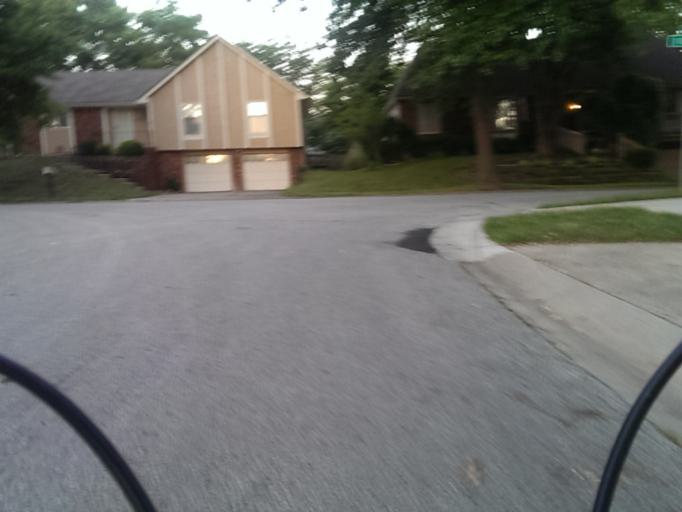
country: US
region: Missouri
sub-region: Jackson County
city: Grandview
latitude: 38.9122
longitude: -94.5799
